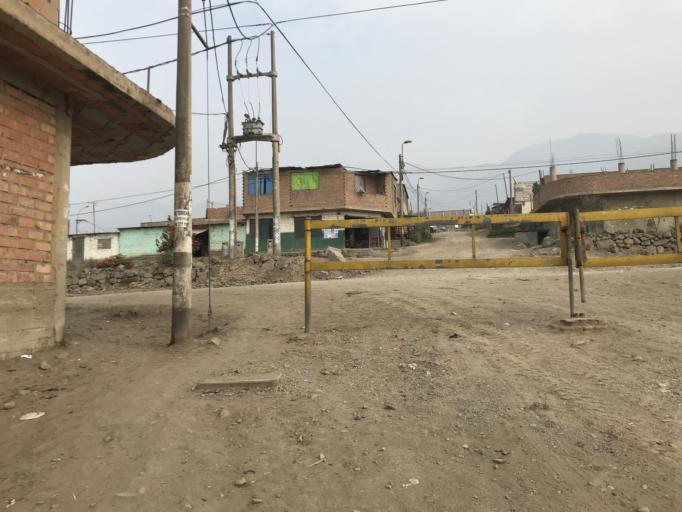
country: PE
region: Lima
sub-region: Lima
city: Carabayllo
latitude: -11.8179
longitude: -77.0447
